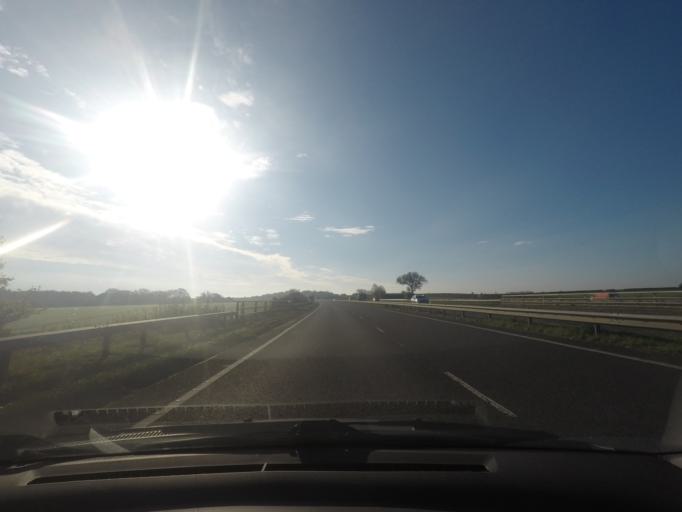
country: GB
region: England
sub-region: North Lincolnshire
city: Barton upon Humber
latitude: 53.6472
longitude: -0.4511
